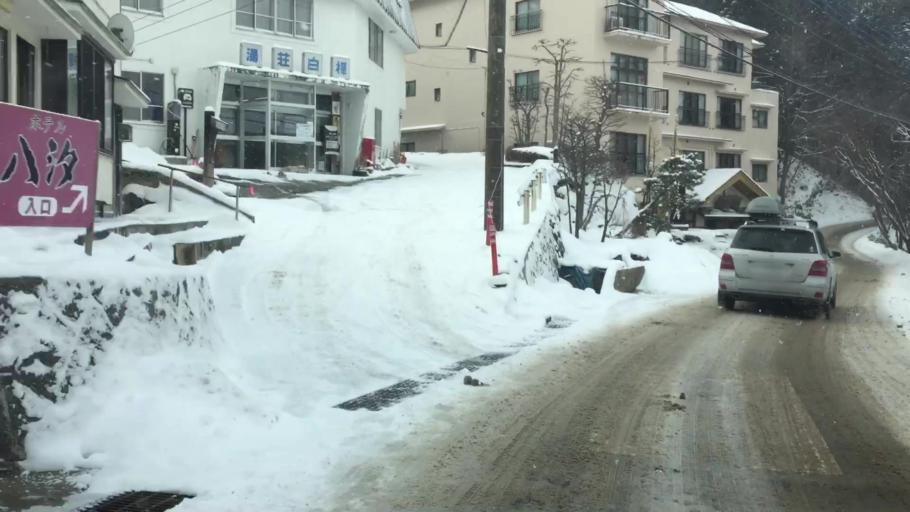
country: JP
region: Tochigi
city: Yaita
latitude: 36.9549
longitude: 139.7794
